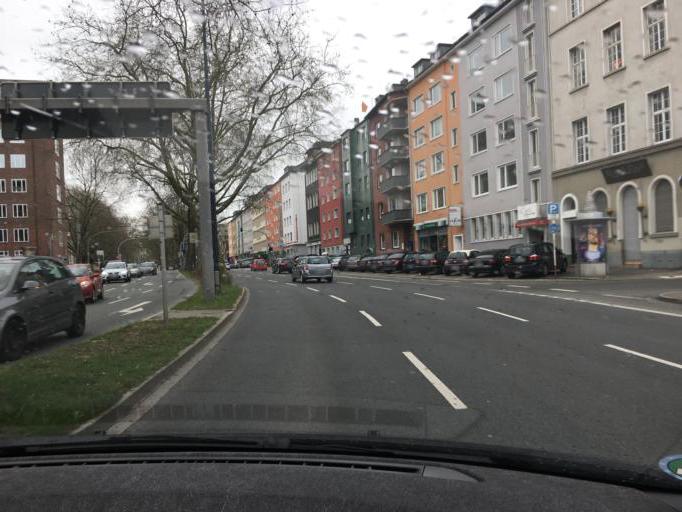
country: DE
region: North Rhine-Westphalia
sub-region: Regierungsbezirk Arnsberg
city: Dortmund
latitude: 51.5133
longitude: 7.4559
